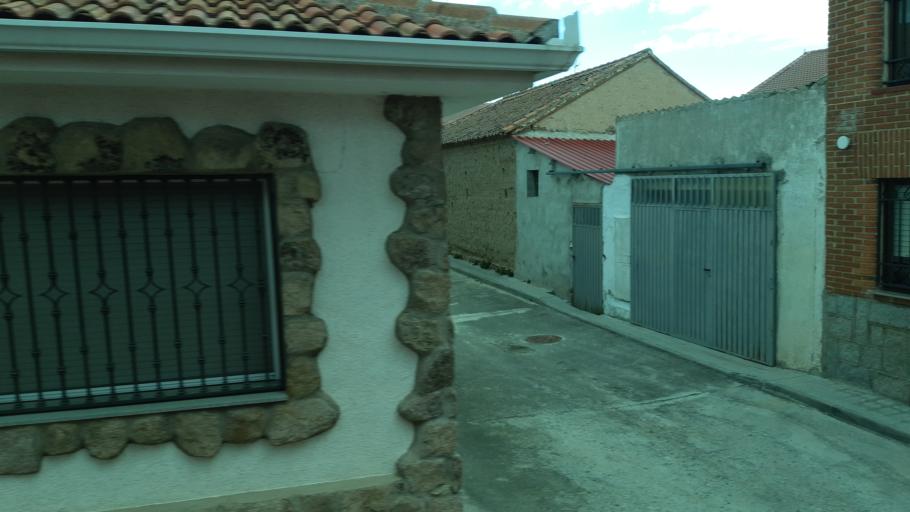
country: ES
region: Castille and Leon
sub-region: Provincia de Segovia
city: Munopedro
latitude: 40.8878
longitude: -4.4727
